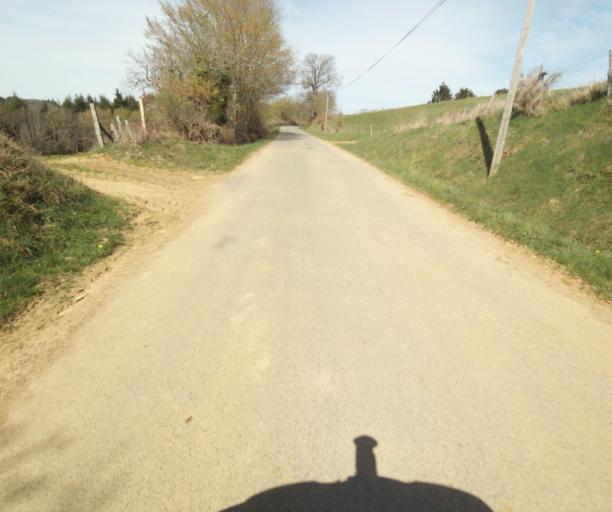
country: FR
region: Limousin
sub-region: Departement de la Correze
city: Seilhac
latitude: 45.3901
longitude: 1.7812
